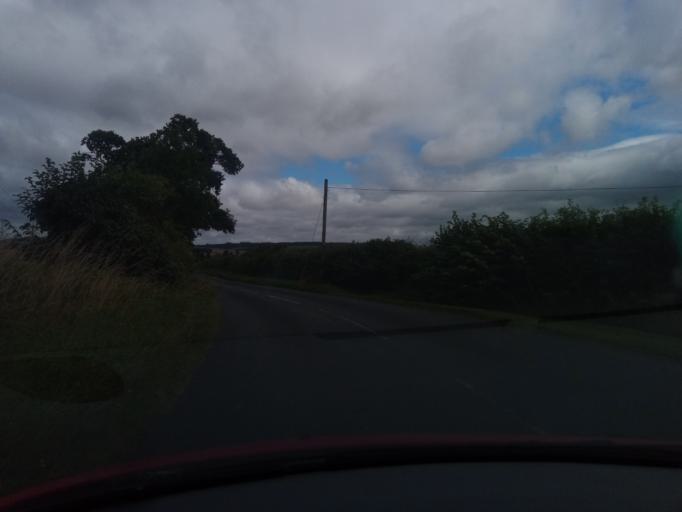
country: GB
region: Scotland
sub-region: The Scottish Borders
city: Kelso
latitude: 55.5258
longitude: -2.4647
